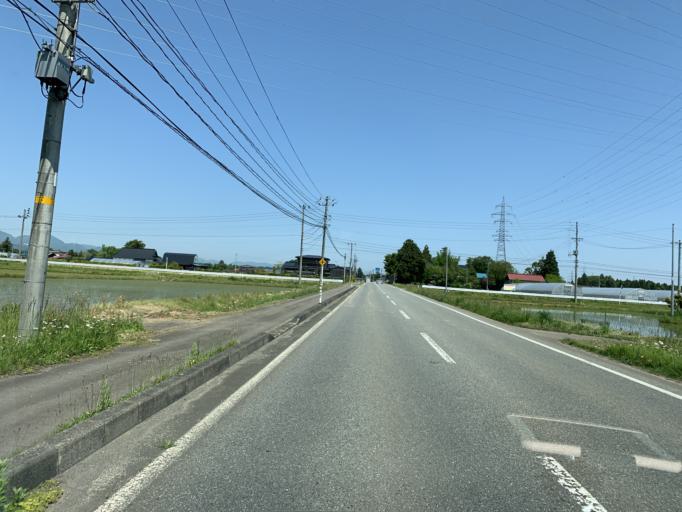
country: JP
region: Iwate
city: Mizusawa
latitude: 39.1779
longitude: 141.0806
